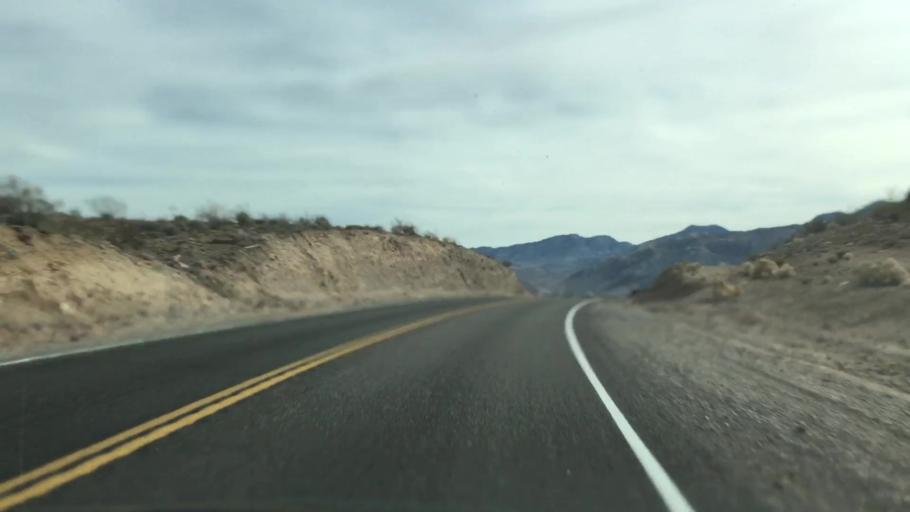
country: US
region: Nevada
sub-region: Nye County
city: Beatty
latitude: 36.9036
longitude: -116.7856
